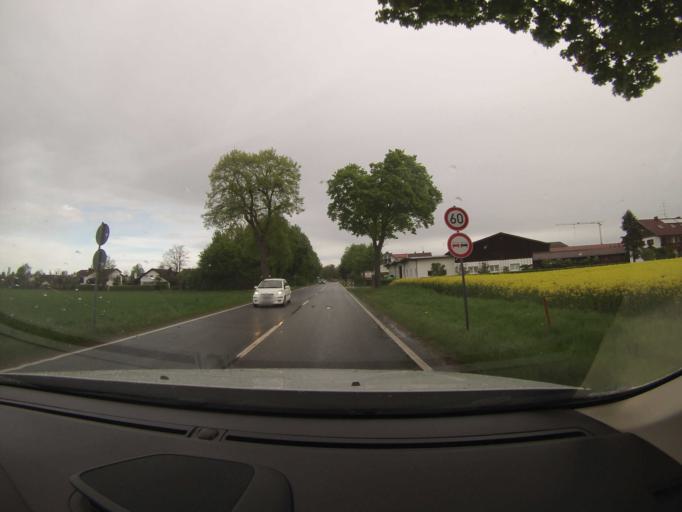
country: DE
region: Bavaria
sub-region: Upper Bavaria
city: Taufkirchen
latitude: 48.0383
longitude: 11.6314
